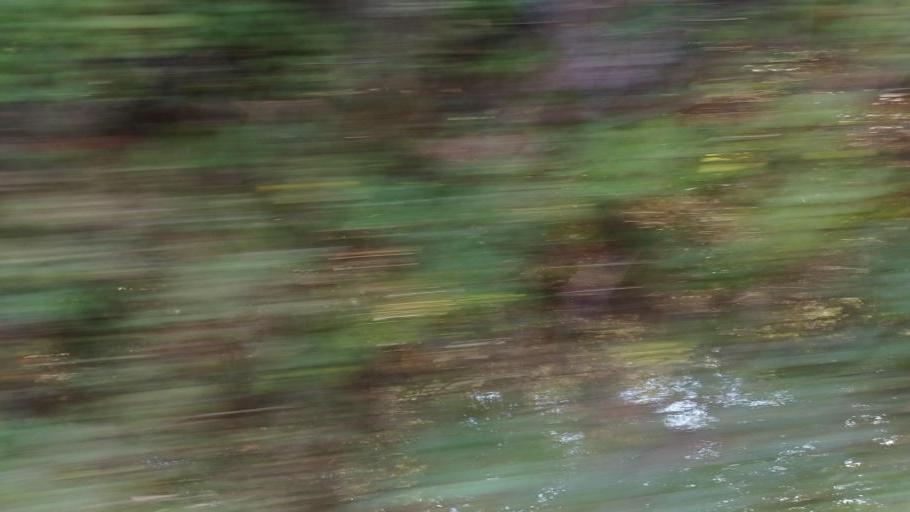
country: CY
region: Pafos
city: Pegeia
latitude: 34.9367
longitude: 32.4590
